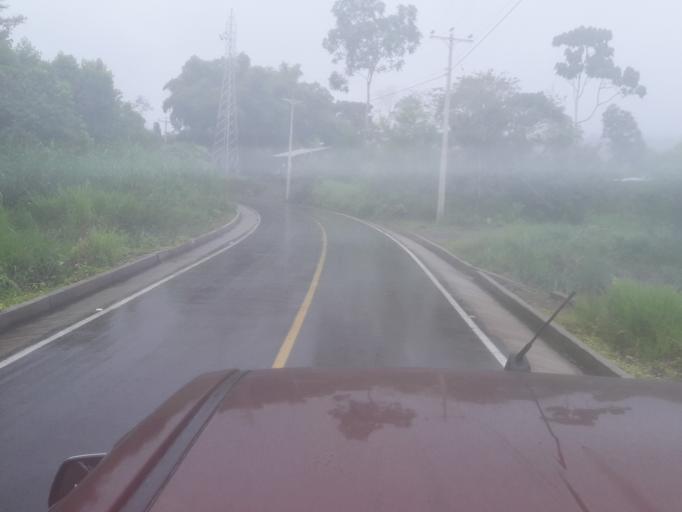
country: EC
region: Napo
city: Tena
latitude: -1.0239
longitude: -77.6668
